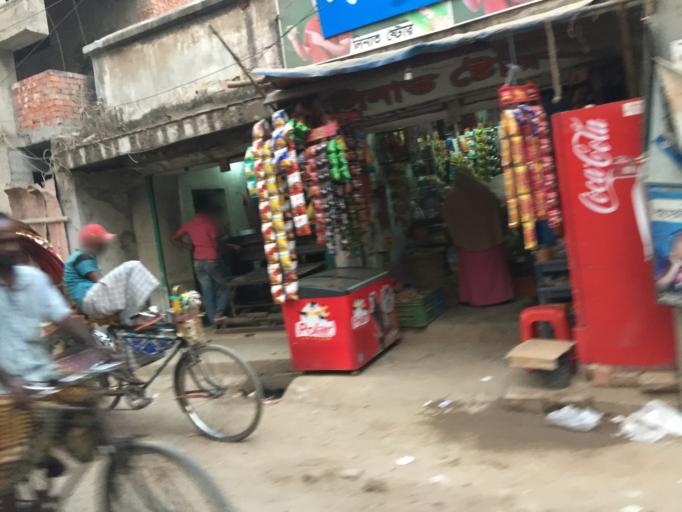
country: BD
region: Dhaka
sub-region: Dhaka
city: Dhaka
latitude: 23.7167
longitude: 90.4025
